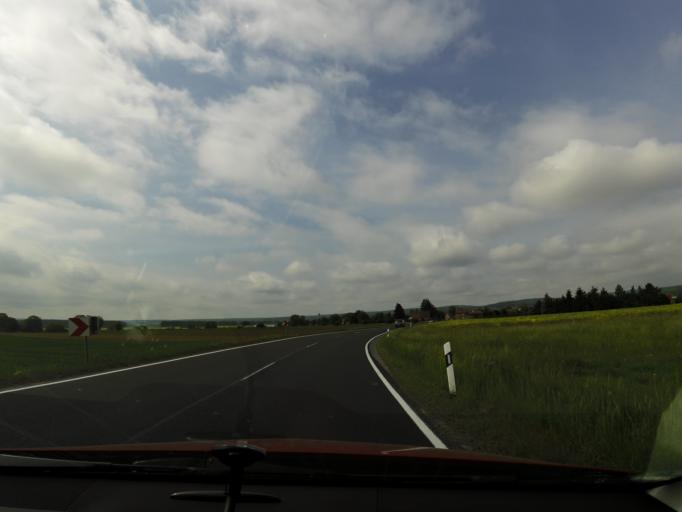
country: DE
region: Thuringia
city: Langula
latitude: 51.1545
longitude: 10.4282
